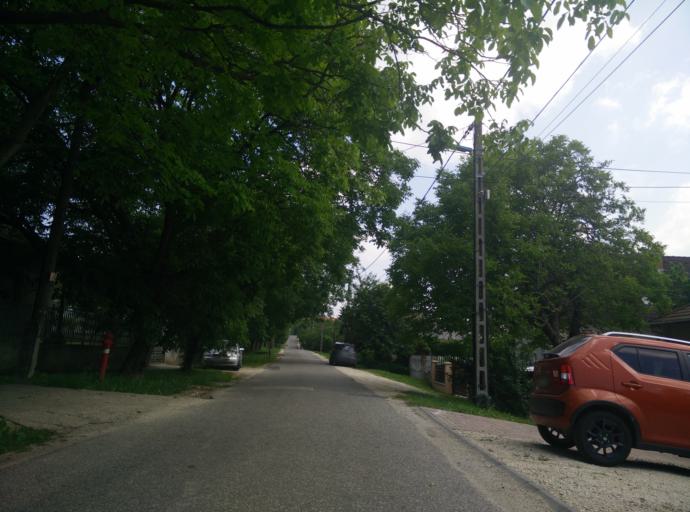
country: HU
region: Pest
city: Biatorbagy
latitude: 47.4660
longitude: 18.8146
